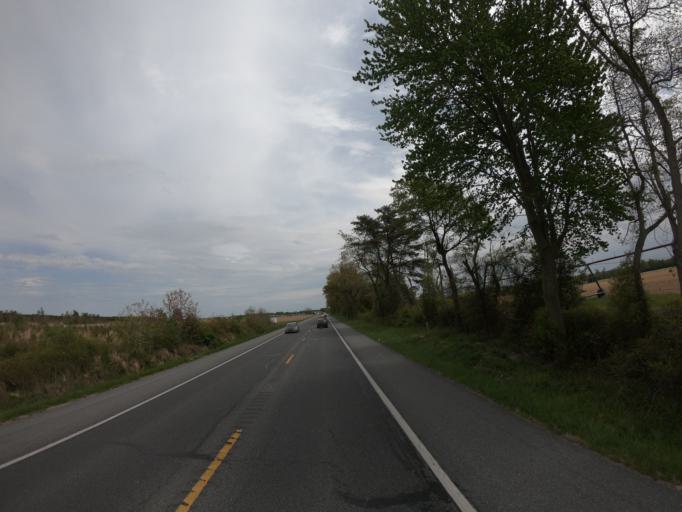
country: US
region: Delaware
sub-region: Sussex County
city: Milton
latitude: 38.7872
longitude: -75.3641
